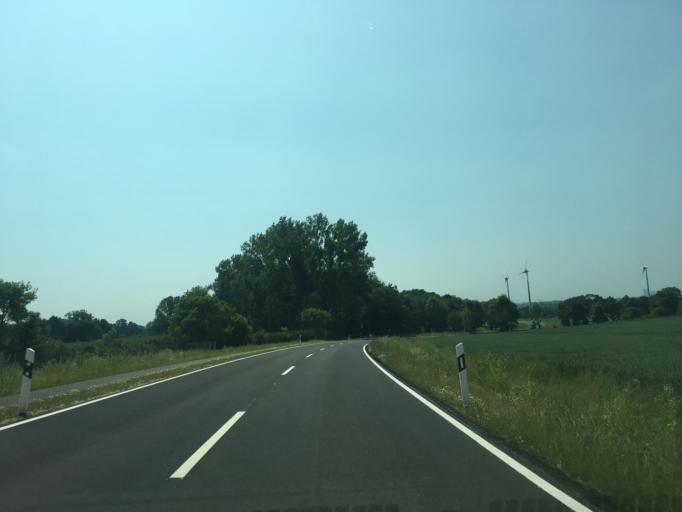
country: DE
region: North Rhine-Westphalia
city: Olfen
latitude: 51.7353
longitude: 7.4026
